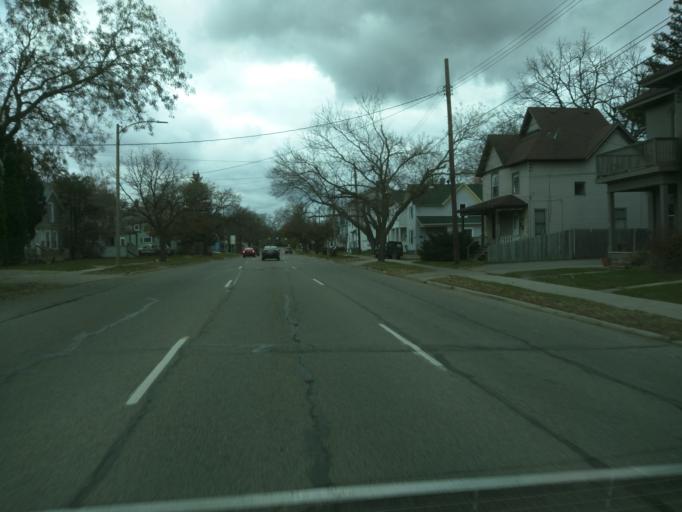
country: US
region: Michigan
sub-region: Ingham County
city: Lansing
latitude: 42.7435
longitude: -84.5539
